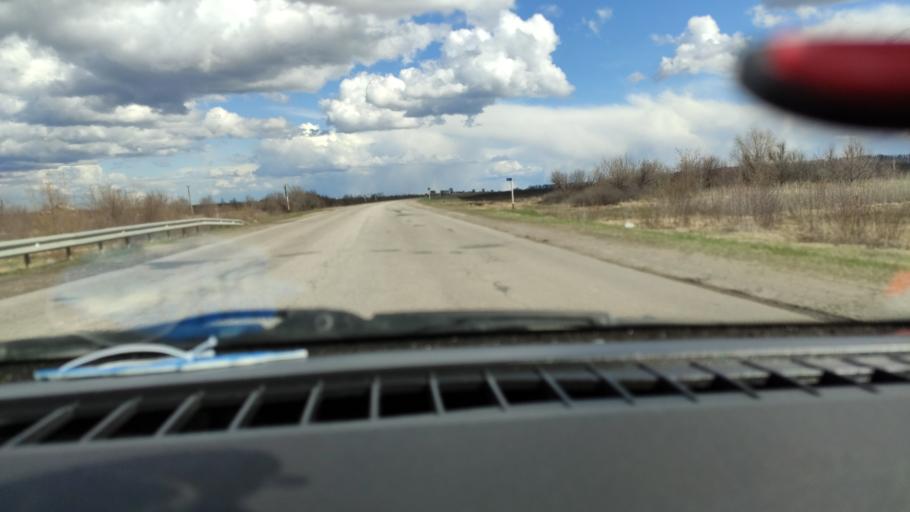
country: RU
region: Samara
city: Varlamovo
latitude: 53.1205
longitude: 48.3274
